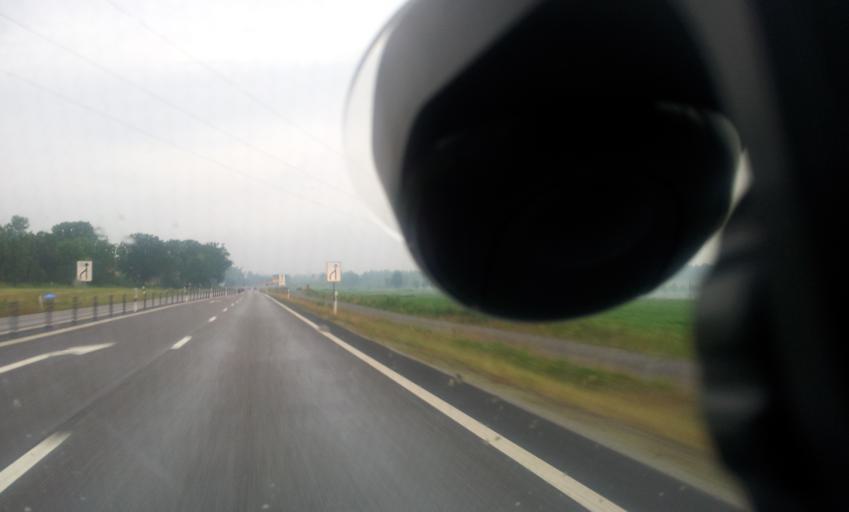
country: SE
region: Kalmar
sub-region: Vasterviks Kommun
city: Vaestervik
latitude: 57.7742
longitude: 16.5479
